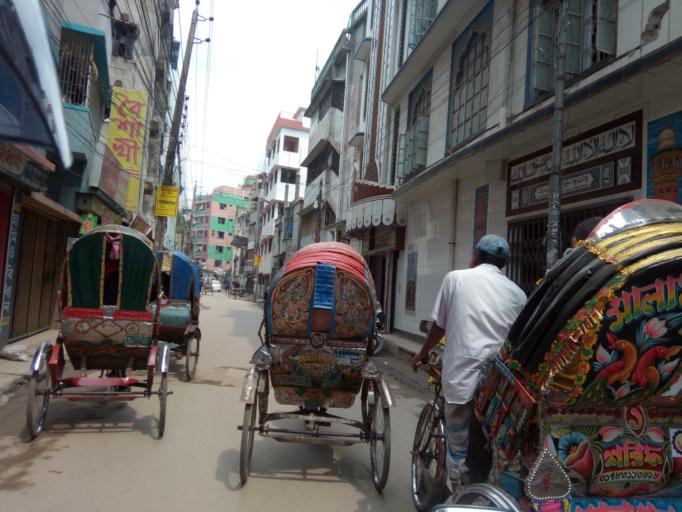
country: BD
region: Dhaka
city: Paltan
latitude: 23.7461
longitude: 90.4283
